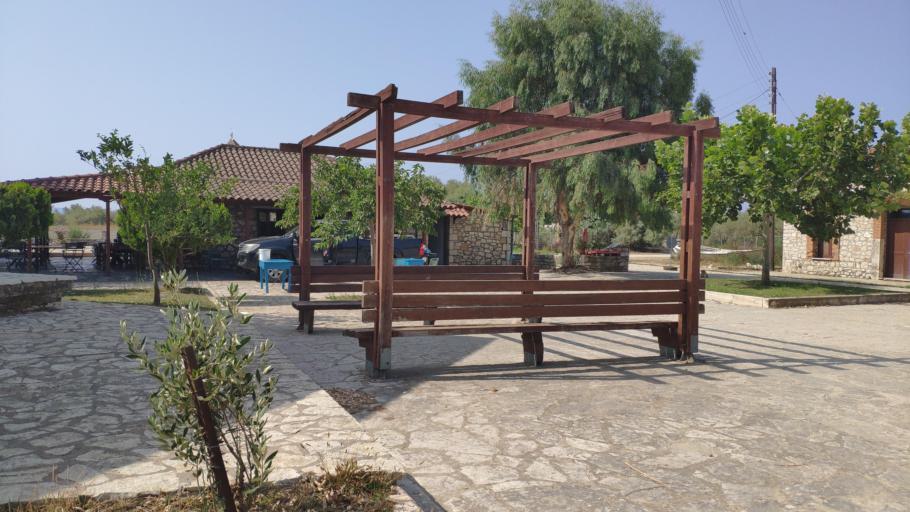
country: GR
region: West Greece
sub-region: Nomos Aitolias kai Akarnanias
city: Menidi
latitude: 39.0385
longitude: 21.0746
